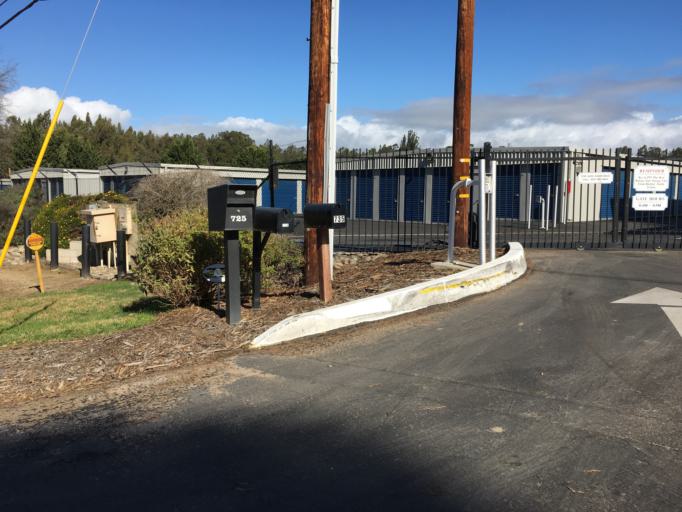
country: US
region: California
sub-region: San Luis Obispo County
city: Callender
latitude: 35.0464
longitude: -120.5768
